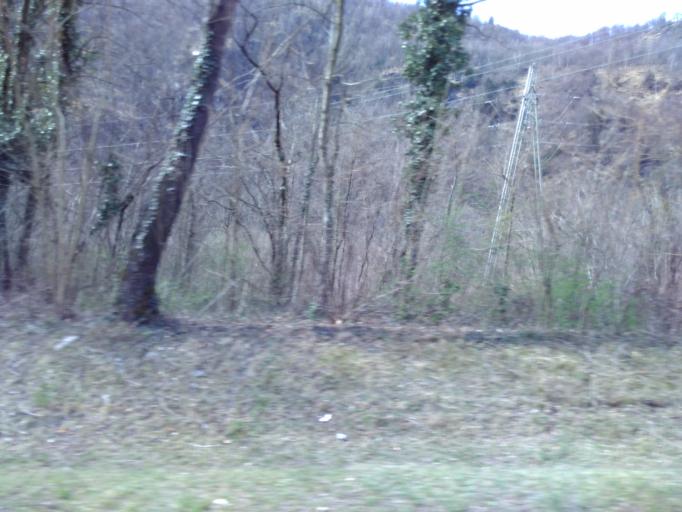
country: CH
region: Ticino
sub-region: Locarno District
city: Verscio
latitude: 46.2014
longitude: 8.7444
